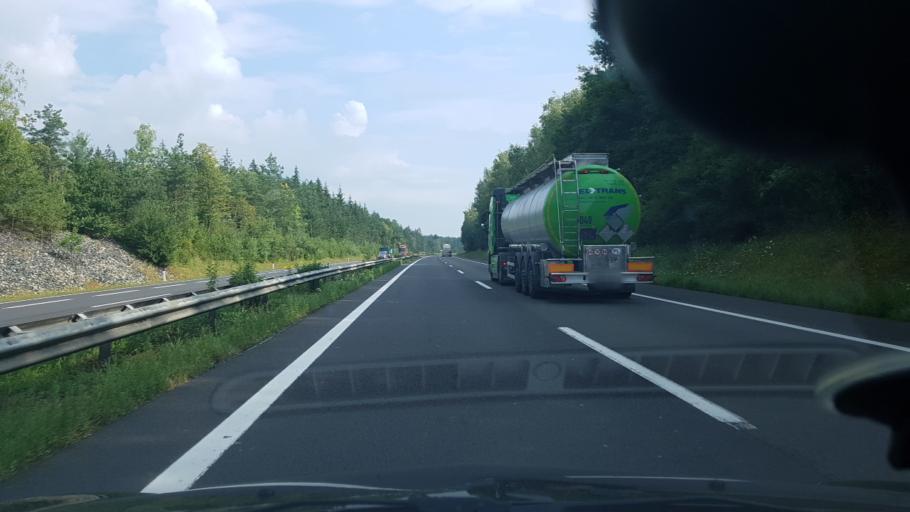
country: AT
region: Styria
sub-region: Politischer Bezirk Hartberg-Fuerstenfeld
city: Hainersdorf
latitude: 47.1222
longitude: 15.9843
